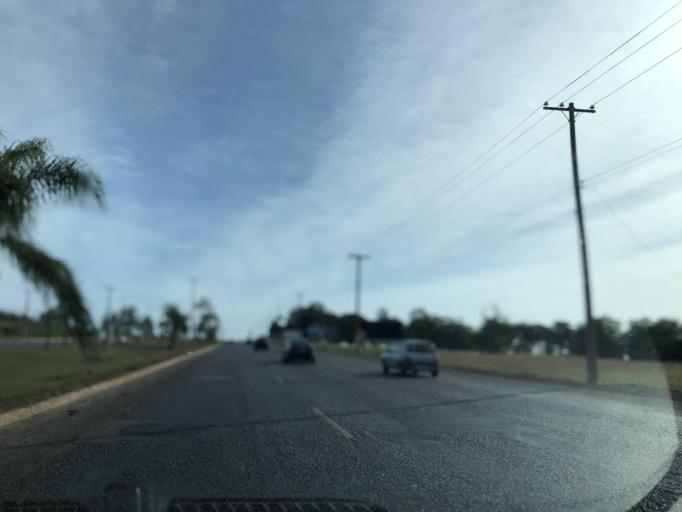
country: BR
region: Federal District
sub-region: Brasilia
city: Brasilia
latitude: -15.8427
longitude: -48.0752
